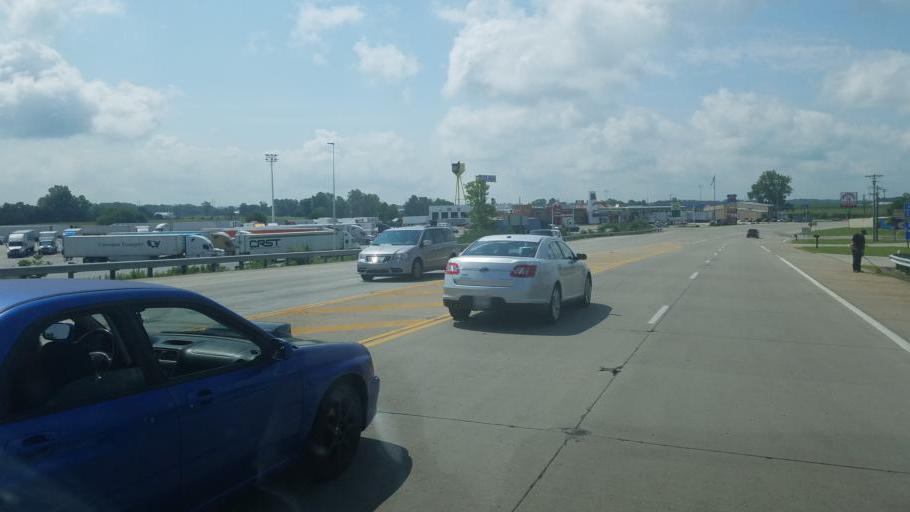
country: US
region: Ohio
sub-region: Fairfield County
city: Millersport
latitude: 39.9413
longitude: -82.5356
